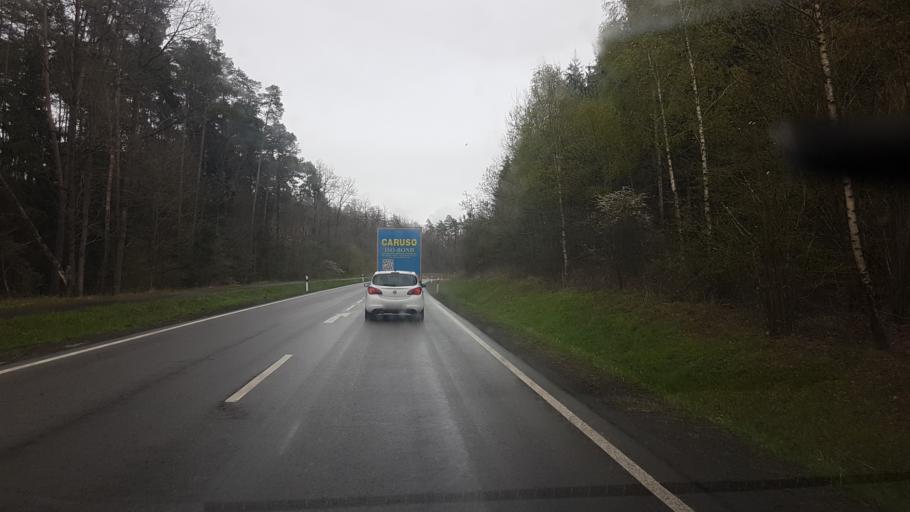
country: DE
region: Bavaria
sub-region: Regierungsbezirk Unterfranken
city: Ermershausen
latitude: 50.2245
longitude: 10.5936
